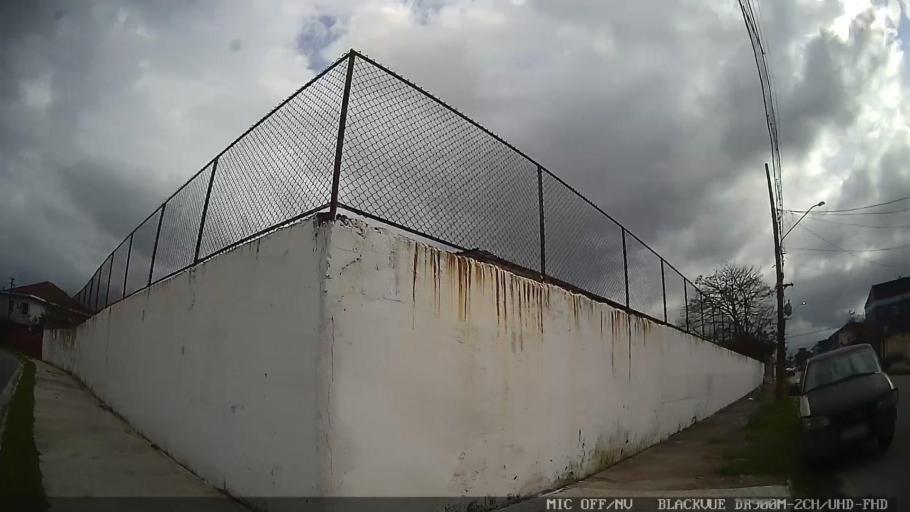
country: BR
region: Sao Paulo
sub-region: Guaruja
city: Guaruja
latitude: -23.9923
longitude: -46.2844
